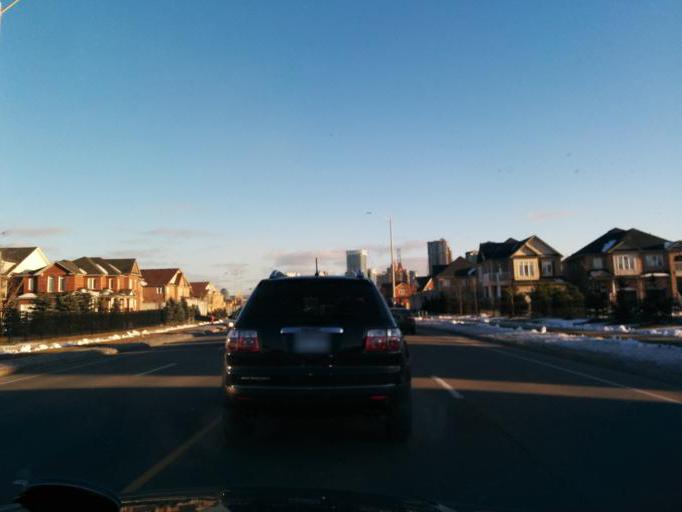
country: CA
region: Ontario
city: Mississauga
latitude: 43.5950
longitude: -79.6603
